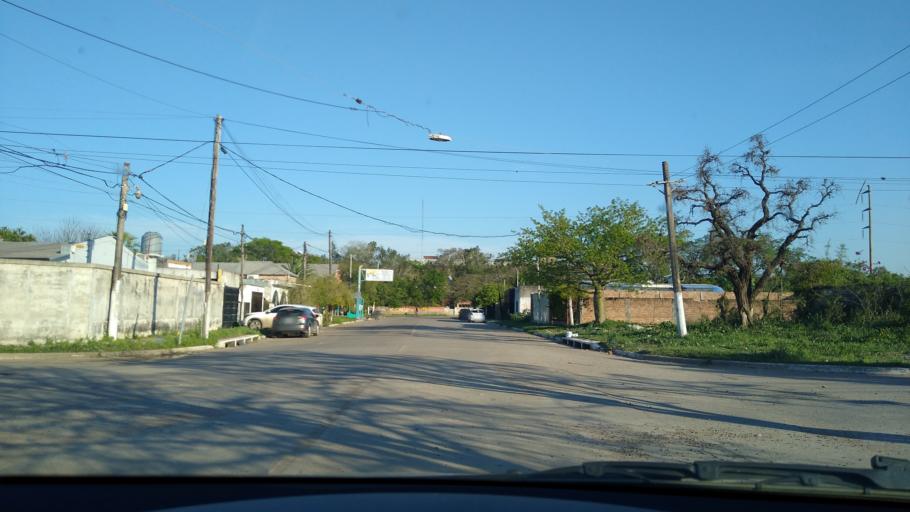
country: AR
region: Chaco
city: Barranqueras
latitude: -27.4892
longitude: -58.9309
